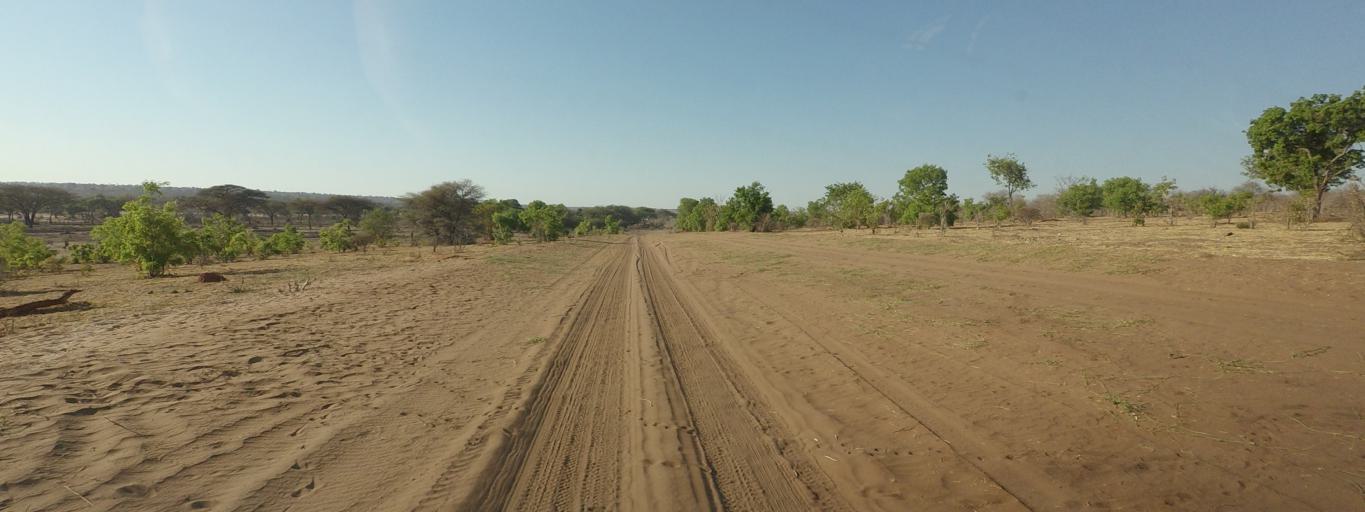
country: BW
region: North West
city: Kasane
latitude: -17.8767
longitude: 25.2344
